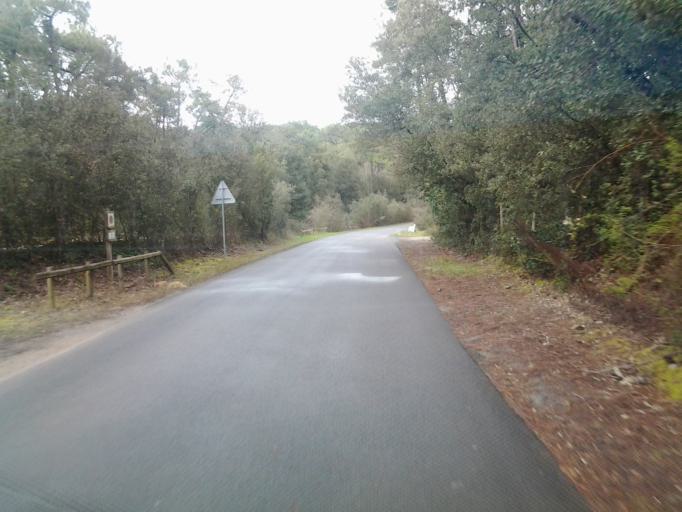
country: FR
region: Pays de la Loire
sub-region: Departement de la Vendee
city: La Tranche-sur-Mer
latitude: 46.3517
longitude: -1.4608
